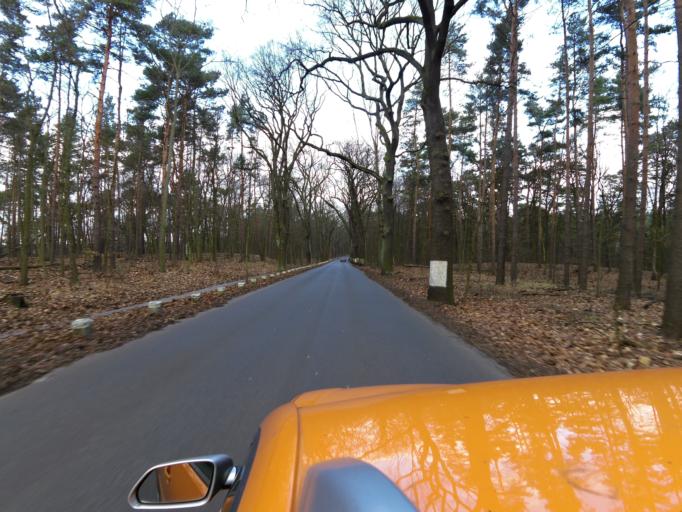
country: DE
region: Berlin
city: Gatow
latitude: 52.4817
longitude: 13.1972
